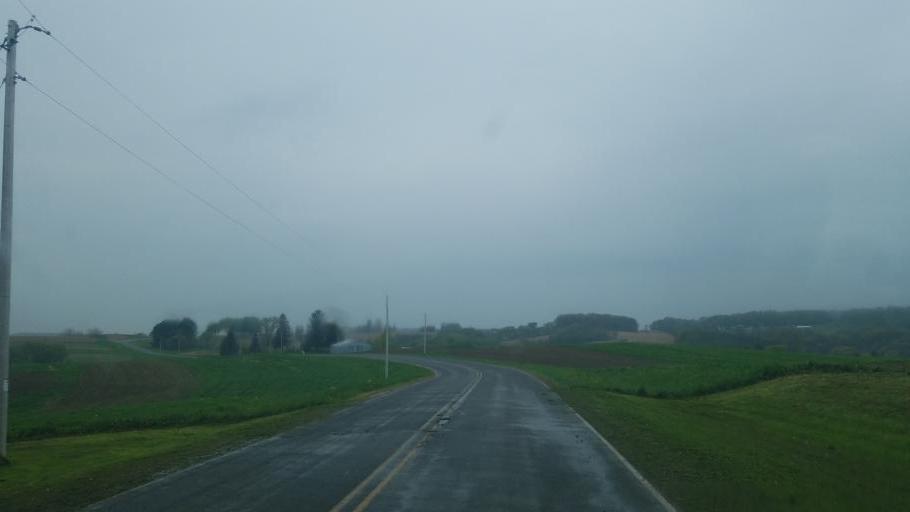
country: US
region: Wisconsin
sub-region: Juneau County
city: Elroy
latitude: 43.6522
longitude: -90.2497
